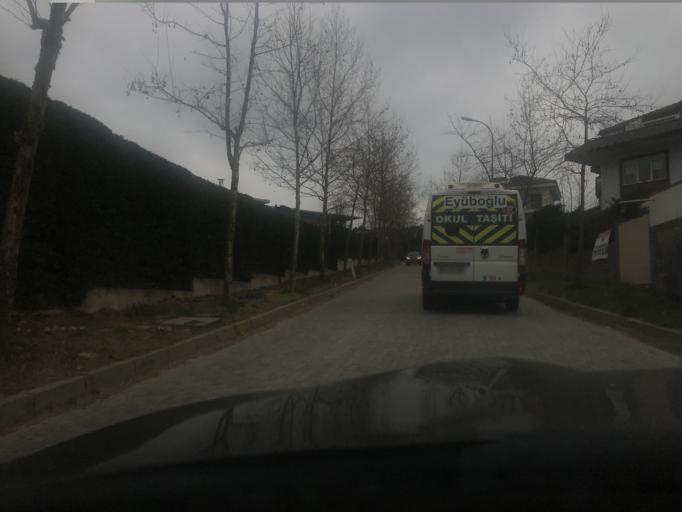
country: TR
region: Istanbul
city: Umraniye
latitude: 41.0445
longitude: 29.1618
